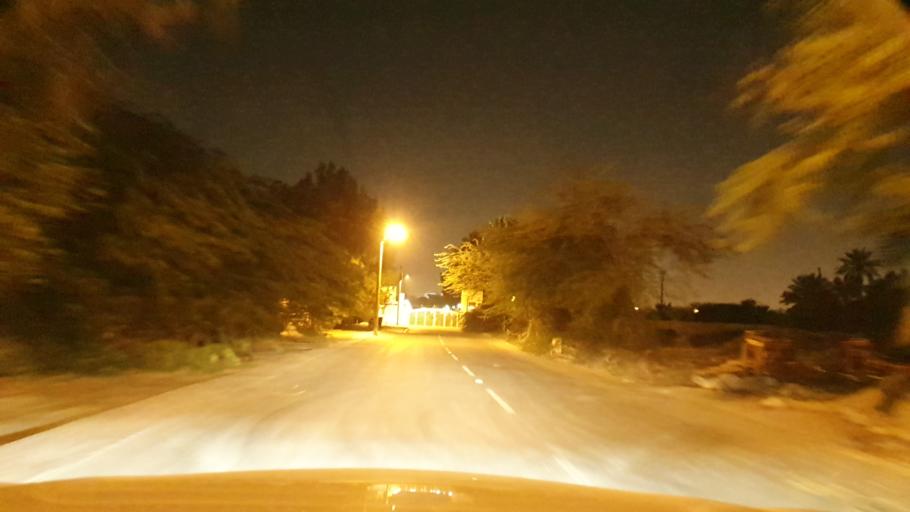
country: BH
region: Manama
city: Jidd Hafs
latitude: 26.2018
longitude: 50.5429
